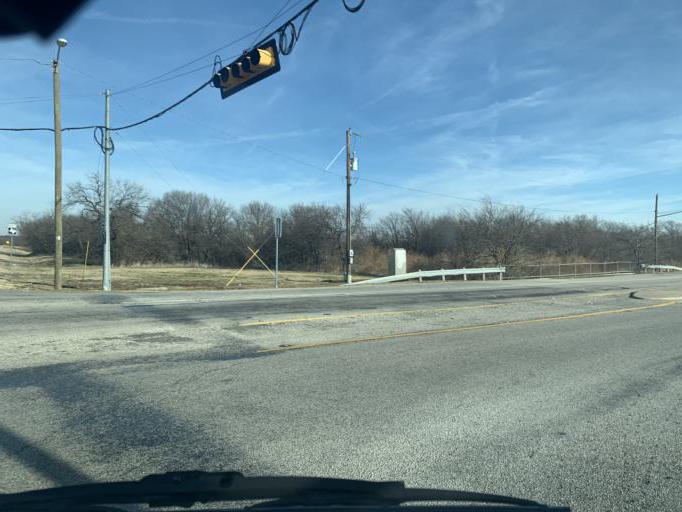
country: US
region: Texas
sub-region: Dallas County
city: Duncanville
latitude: 32.6562
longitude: -96.9795
